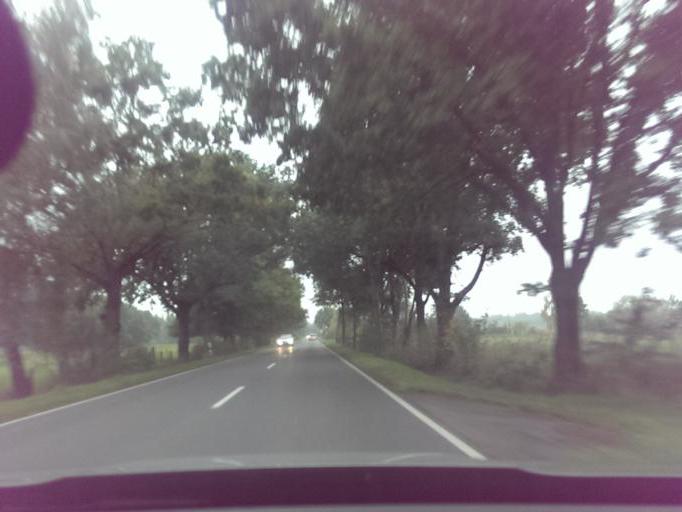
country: DE
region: Lower Saxony
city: Garbsen-Mitte
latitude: 52.4650
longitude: 9.6443
